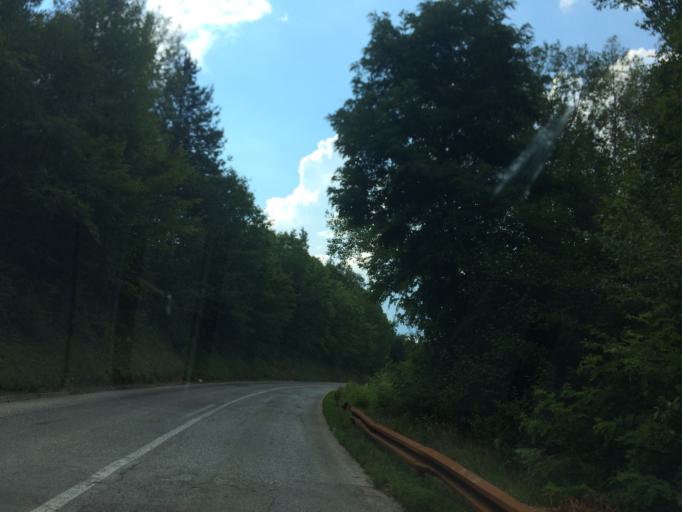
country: RS
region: Central Serbia
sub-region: Zlatiborski Okrug
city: Prijepolje
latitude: 43.3615
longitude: 19.6104
